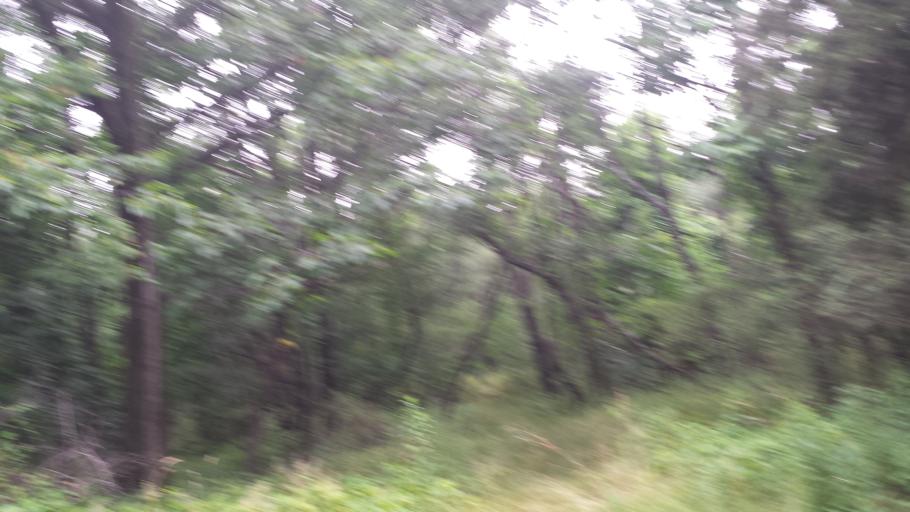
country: US
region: New York
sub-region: Westchester County
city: Crugers
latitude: 41.2343
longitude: -73.9369
